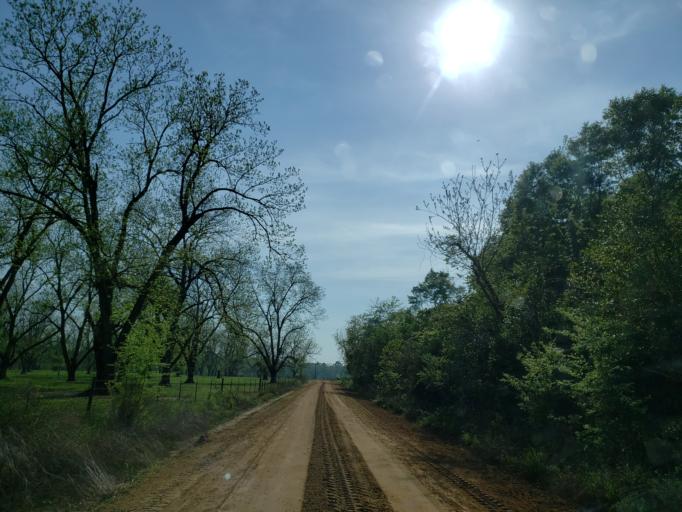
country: US
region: Georgia
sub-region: Dooly County
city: Vienna
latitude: 32.1073
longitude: -83.7800
